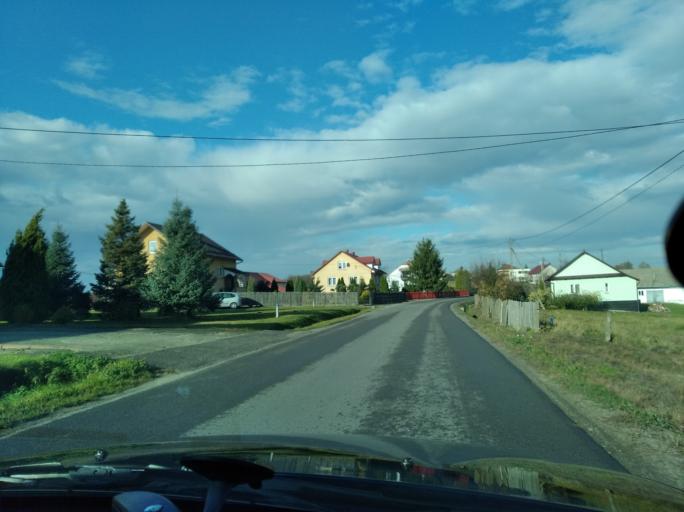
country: PL
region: Subcarpathian Voivodeship
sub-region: Powiat ropczycko-sedziszowski
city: Niedzwiada
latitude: 50.0055
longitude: 21.4628
